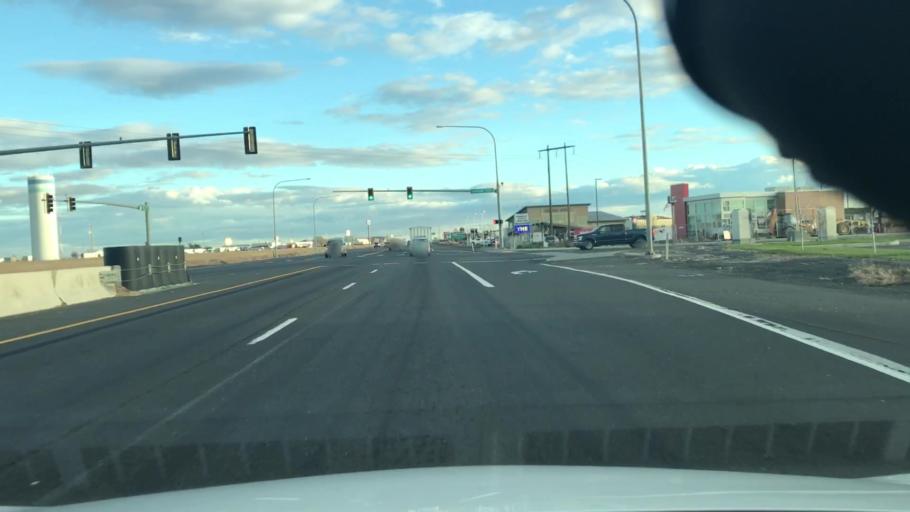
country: US
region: Washington
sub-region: Grant County
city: Moses Lake
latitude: 47.1066
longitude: -119.2525
